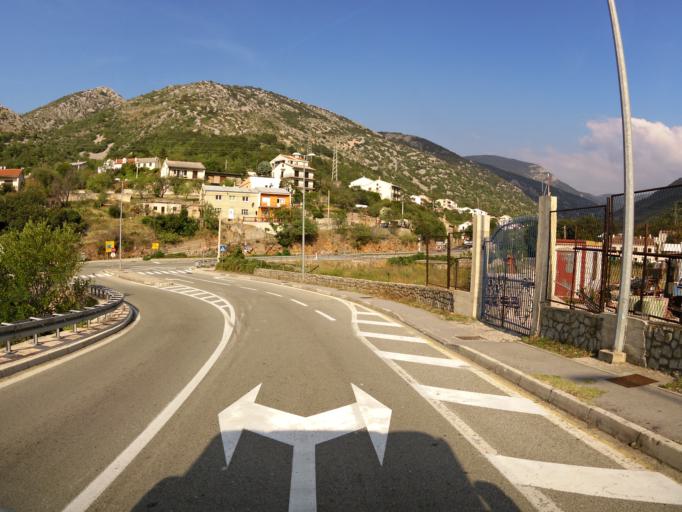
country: HR
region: Licko-Senjska
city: Senj
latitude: 44.9862
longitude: 14.9098
